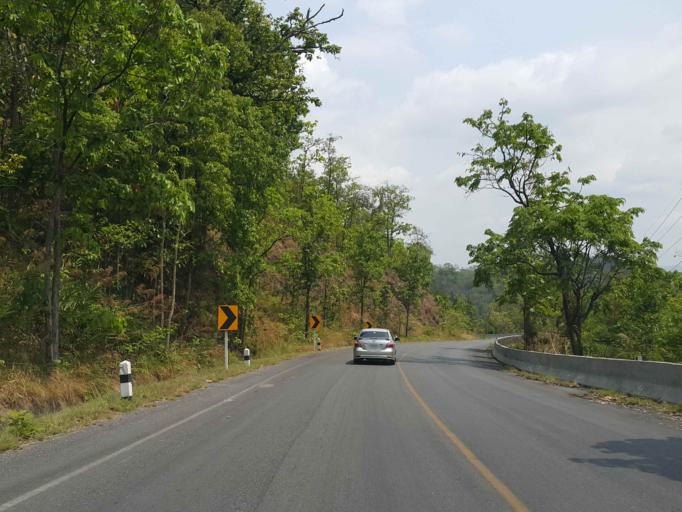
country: TH
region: Lampang
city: Thoen
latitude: 17.6199
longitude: 99.3169
